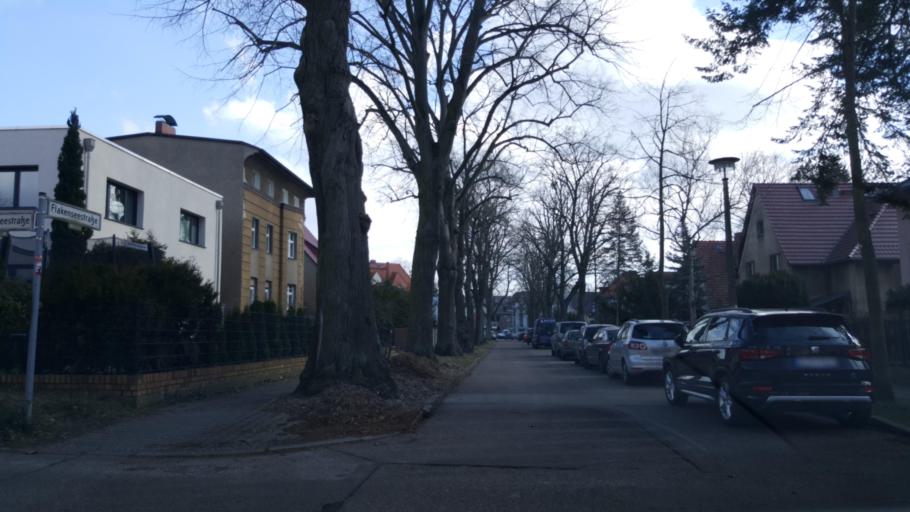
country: DE
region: Berlin
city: Friedrichshagen
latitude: 52.4498
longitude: 13.6362
